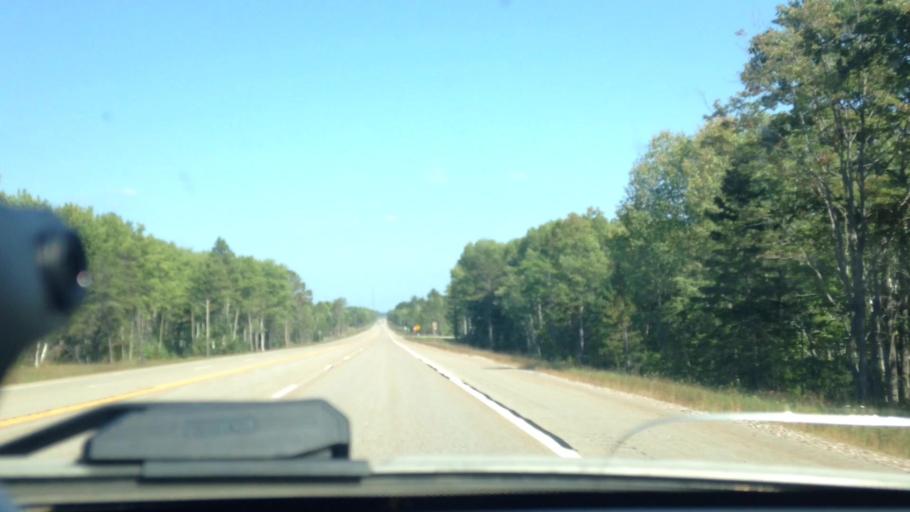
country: US
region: Michigan
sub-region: Chippewa County
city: Sault Ste. Marie
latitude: 46.3643
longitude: -84.7648
